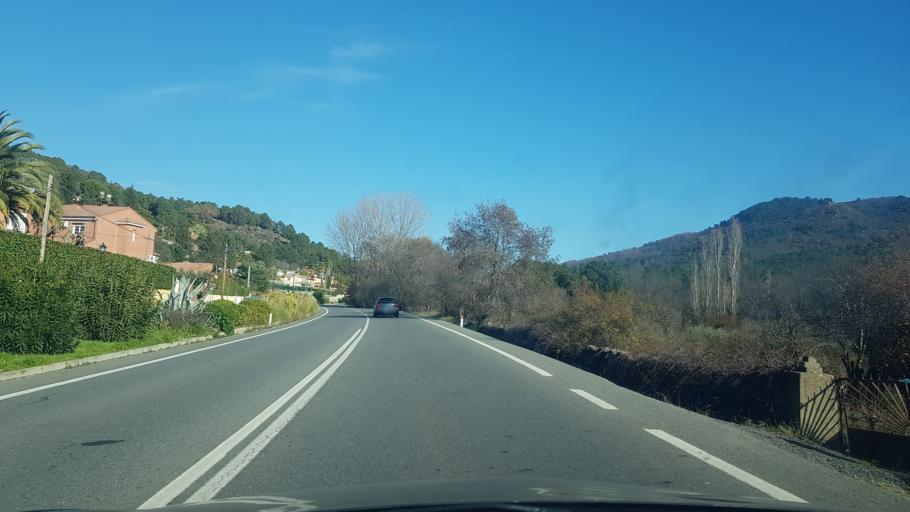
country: ES
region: Castille and Leon
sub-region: Provincia de Avila
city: Casillas
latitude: 40.3034
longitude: -4.5398
